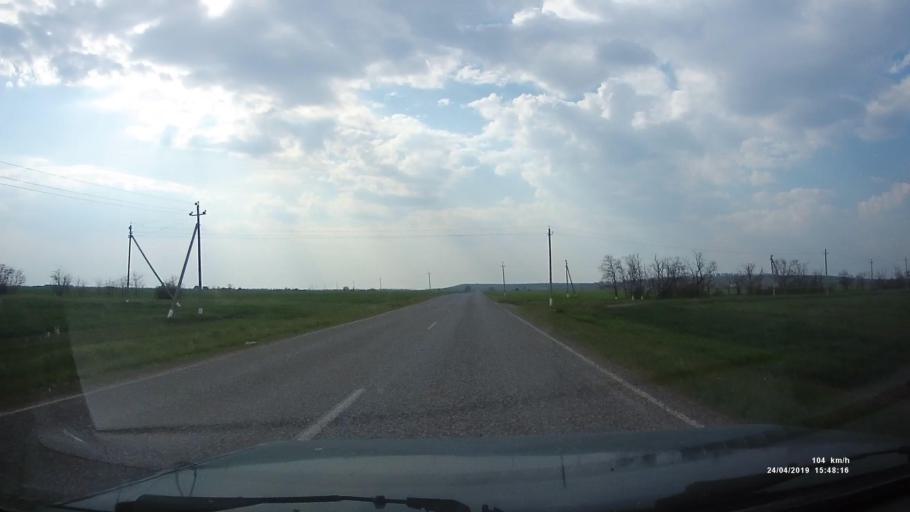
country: RU
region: Kalmykiya
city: Yashalta
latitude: 46.5977
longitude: 42.6795
